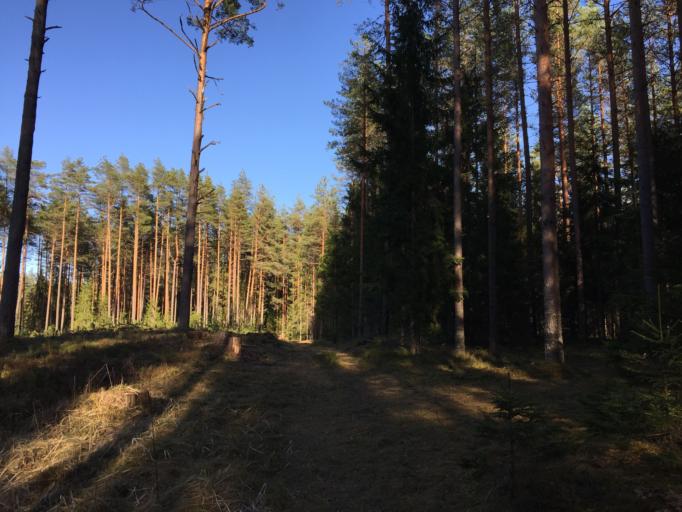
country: LV
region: Valkas Rajons
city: Valka
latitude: 57.7971
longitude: 25.9580
